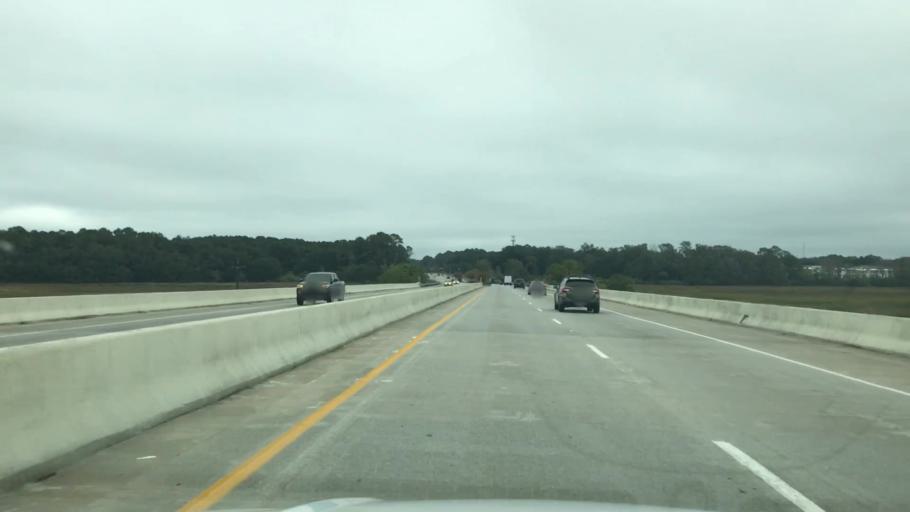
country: US
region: South Carolina
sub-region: Beaufort County
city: Shell Point
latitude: 32.3910
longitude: -80.7733
